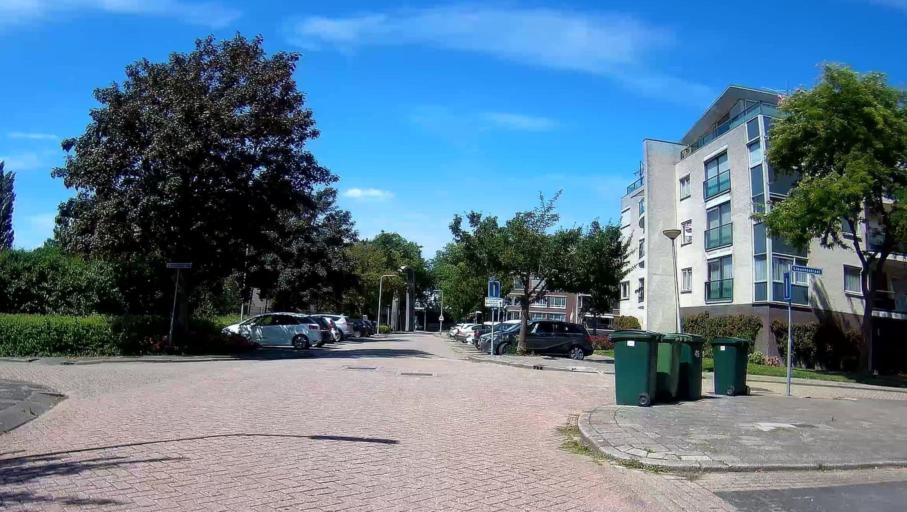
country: NL
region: South Holland
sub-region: Gemeente Krimpen aan den IJssel
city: Krimpen aan den IJssel
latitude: 51.9126
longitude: 4.5963
